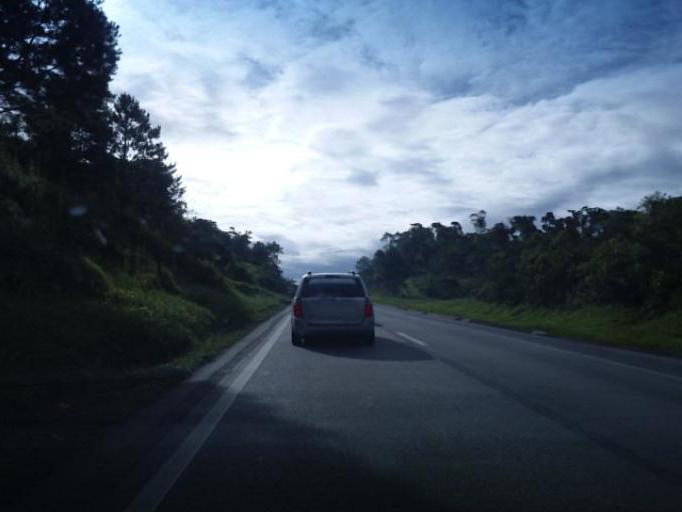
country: BR
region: Parana
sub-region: Antonina
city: Antonina
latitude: -25.1092
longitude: -48.7633
